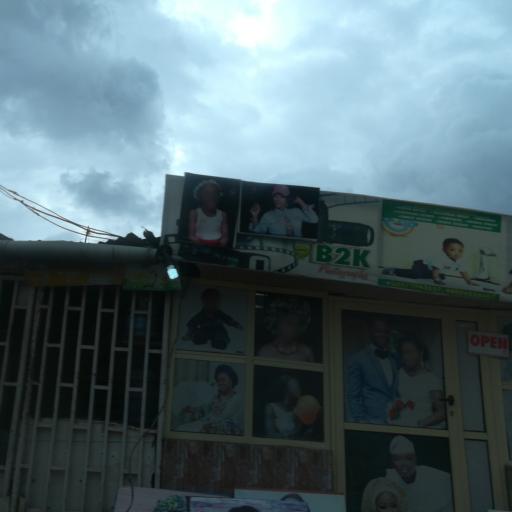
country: NG
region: Lagos
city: Agege
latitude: 6.6099
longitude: 3.2974
